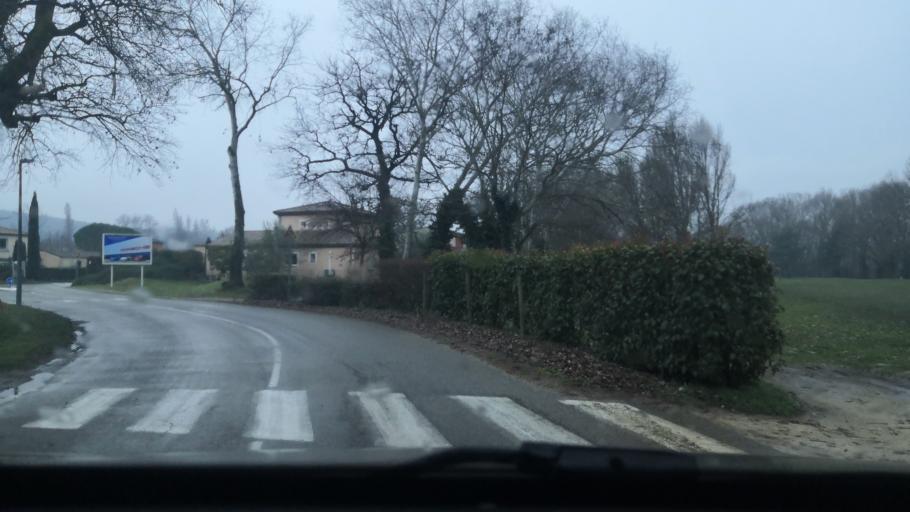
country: FR
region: Rhone-Alpes
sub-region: Departement de la Drome
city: Montboucher-sur-Jabron
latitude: 44.5452
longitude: 4.8027
